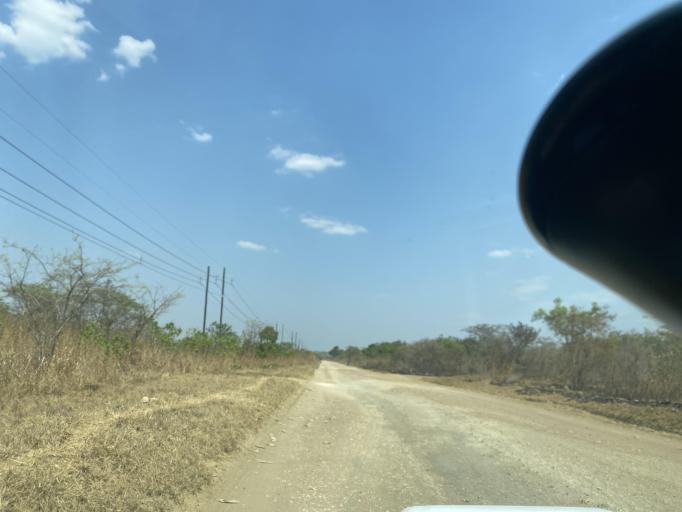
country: ZM
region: Lusaka
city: Lusaka
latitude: -15.3143
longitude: 28.0556
